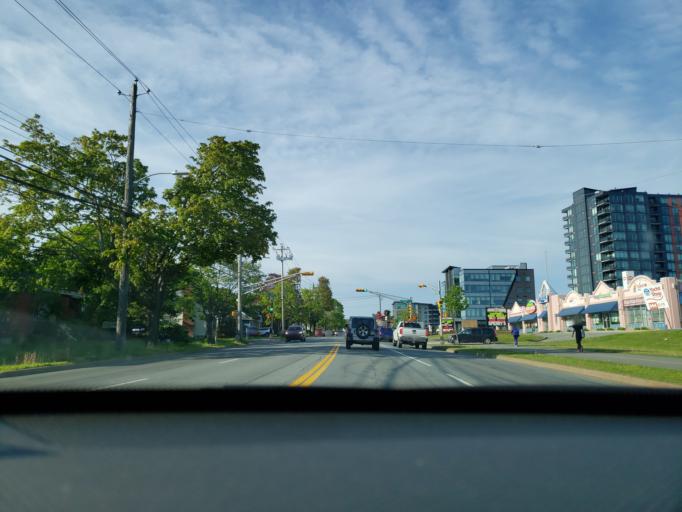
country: CA
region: Nova Scotia
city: Dartmouth
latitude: 44.6568
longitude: -63.6296
